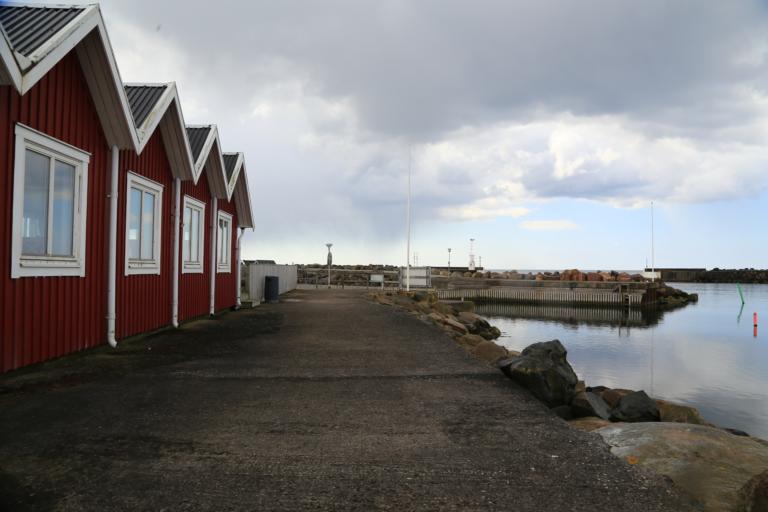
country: SE
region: Halland
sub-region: Varbergs Kommun
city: Traslovslage
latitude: 57.0574
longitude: 12.2702
